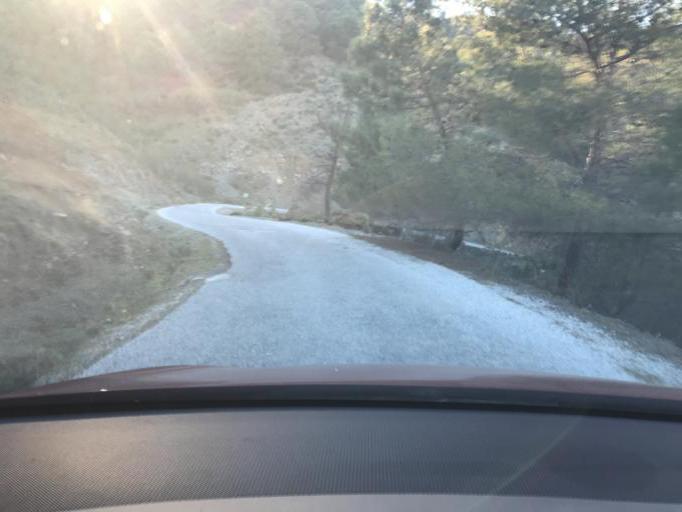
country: ES
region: Andalusia
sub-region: Provincia de Malaga
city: Tolox
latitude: 36.6823
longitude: -4.9133
